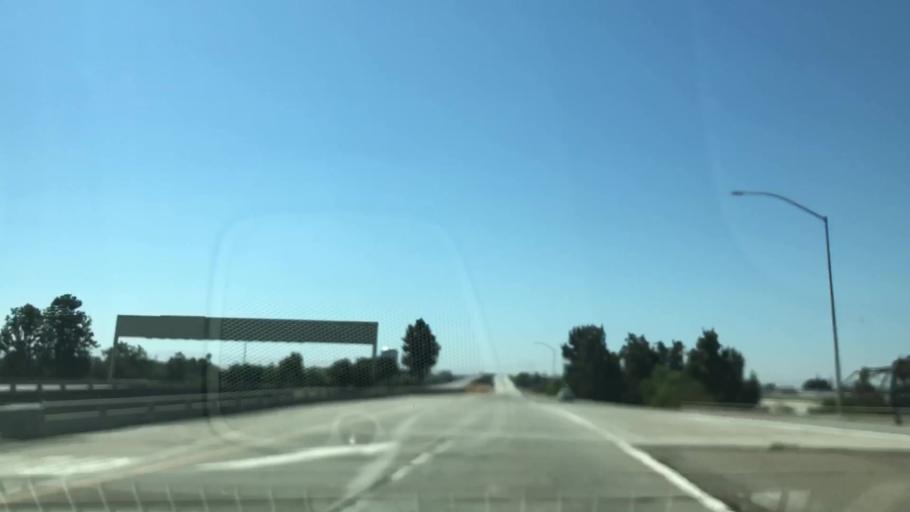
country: US
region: California
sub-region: San Joaquin County
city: Stockton
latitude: 37.9464
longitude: -121.3067
